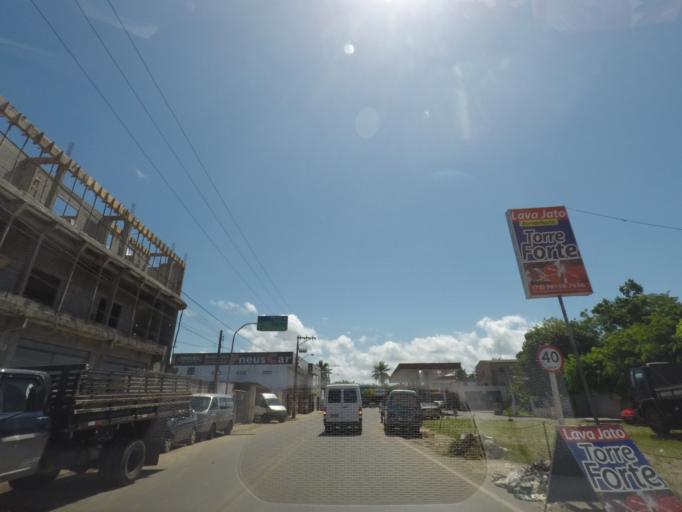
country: BR
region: Bahia
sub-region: Valenca
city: Valenca
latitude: -13.3760
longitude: -39.0740
